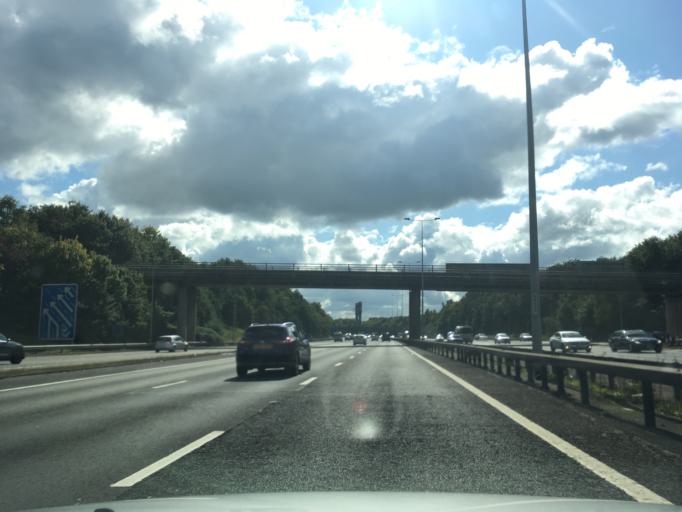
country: GB
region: England
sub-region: Surrey
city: Chertsey
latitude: 51.3974
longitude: -0.5355
